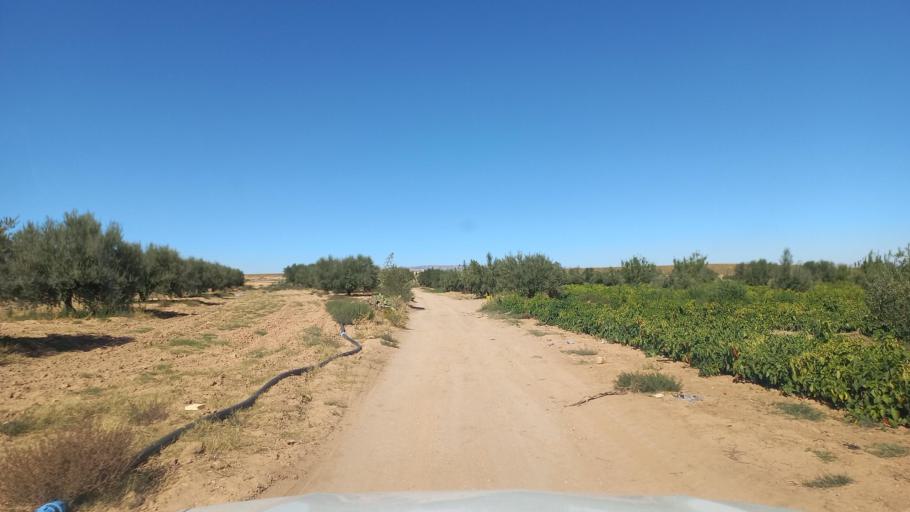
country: TN
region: Al Qasrayn
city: Sbiba
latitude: 35.4036
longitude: 9.0879
